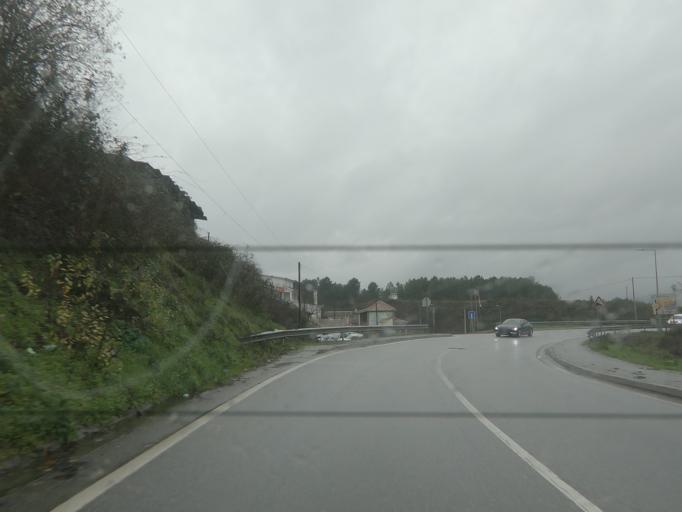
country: PT
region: Vila Real
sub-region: Vila Real
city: Vila Real
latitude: 41.2794
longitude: -7.7202
